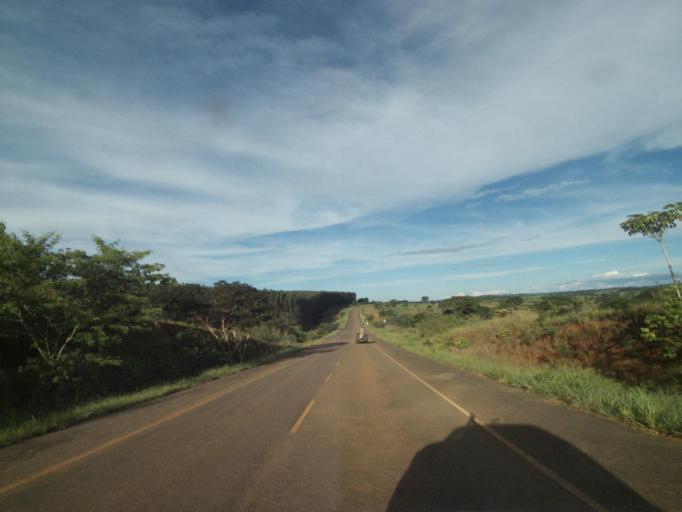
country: BR
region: Goias
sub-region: Jaragua
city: Jaragua
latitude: -15.8847
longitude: -49.4492
